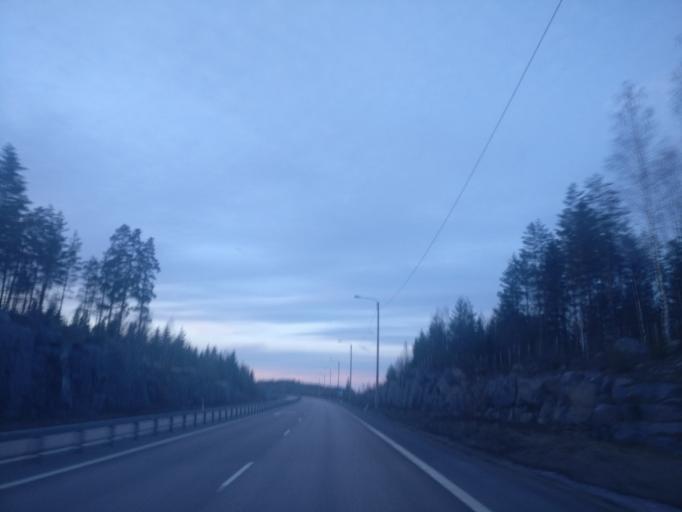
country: FI
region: Central Finland
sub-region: Jyvaeskylae
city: Saeynaetsalo
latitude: 62.1690
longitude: 25.9044
